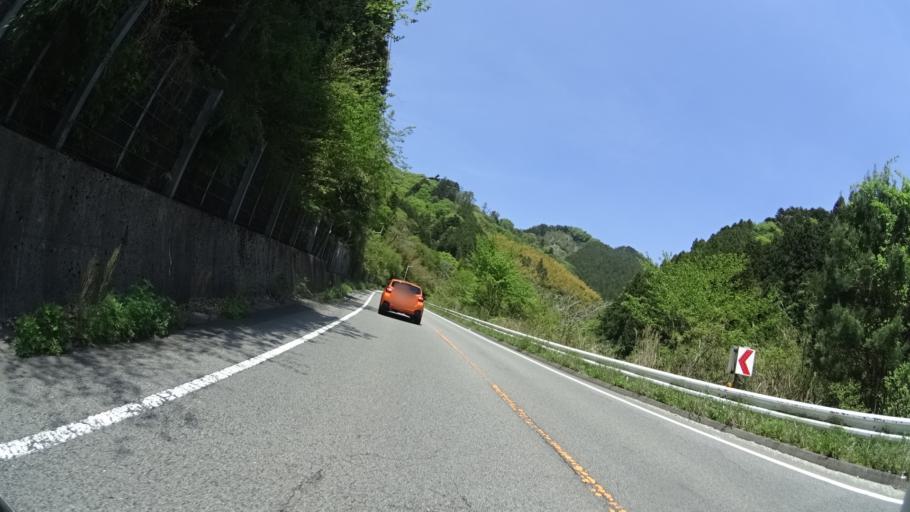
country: JP
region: Ehime
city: Hojo
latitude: 33.9289
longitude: 132.8941
